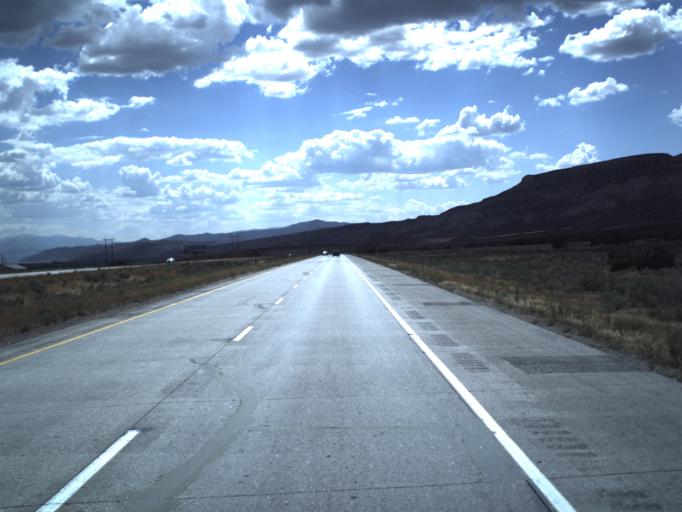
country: US
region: Utah
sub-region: Sevier County
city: Aurora
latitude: 38.8521
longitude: -112.0001
